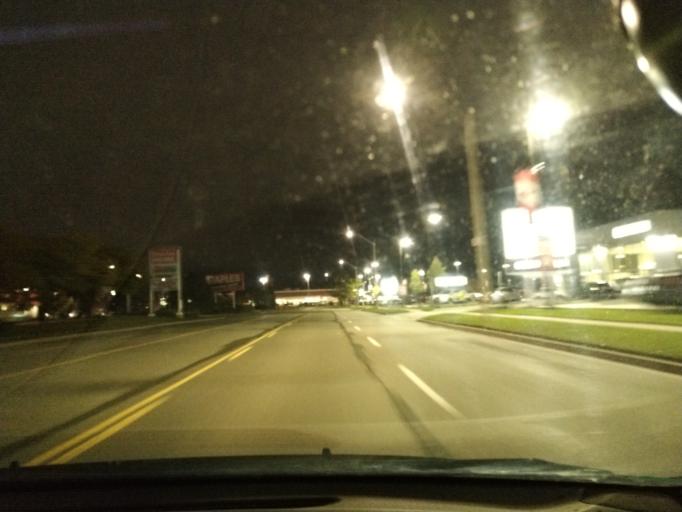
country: CA
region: Ontario
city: Innisfil
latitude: 44.3367
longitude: -79.6879
